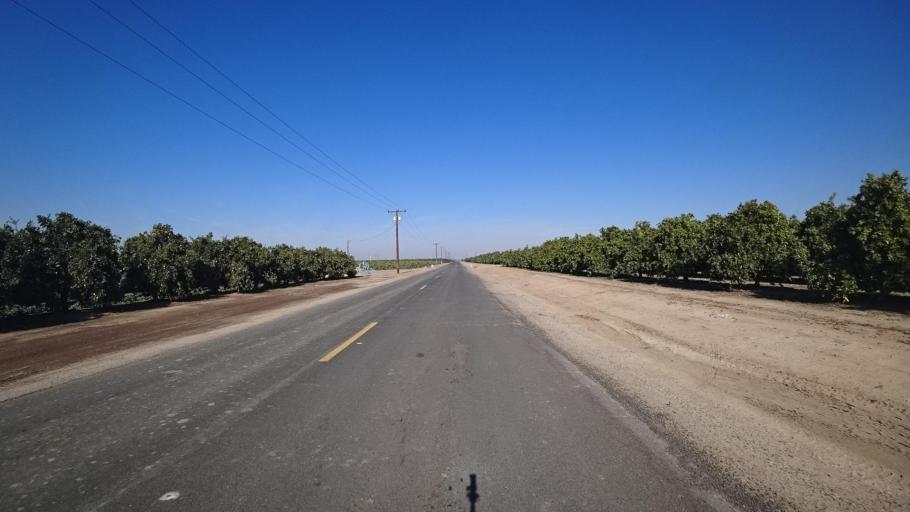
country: US
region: California
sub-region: Tulare County
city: Richgrove
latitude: 35.7280
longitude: -119.1340
